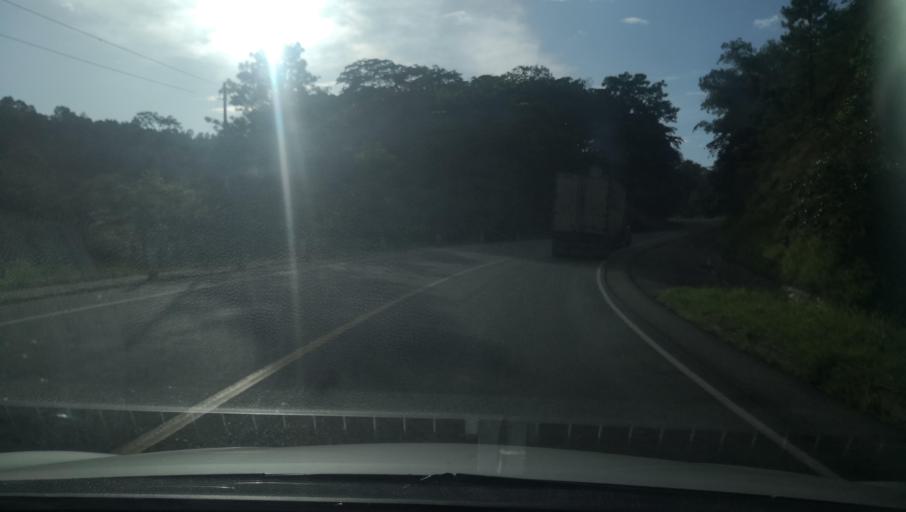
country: NI
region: Nueva Segovia
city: Mozonte
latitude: 13.7266
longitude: -86.5084
